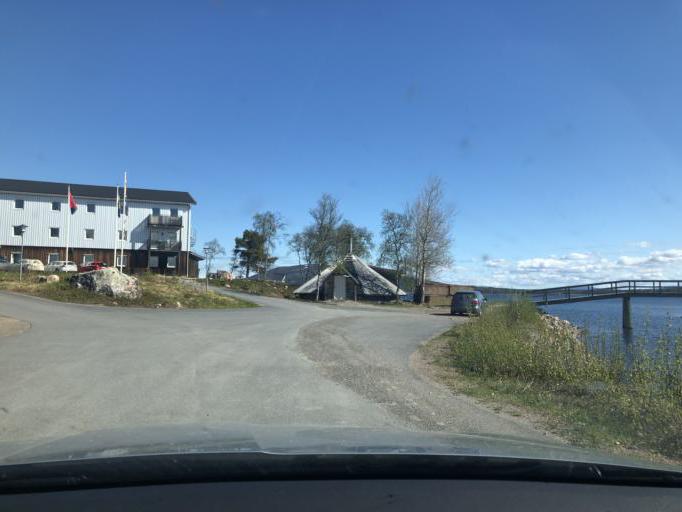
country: SE
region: Norrbotten
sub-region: Arjeplogs Kommun
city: Arjeplog
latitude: 66.0551
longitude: 17.8890
